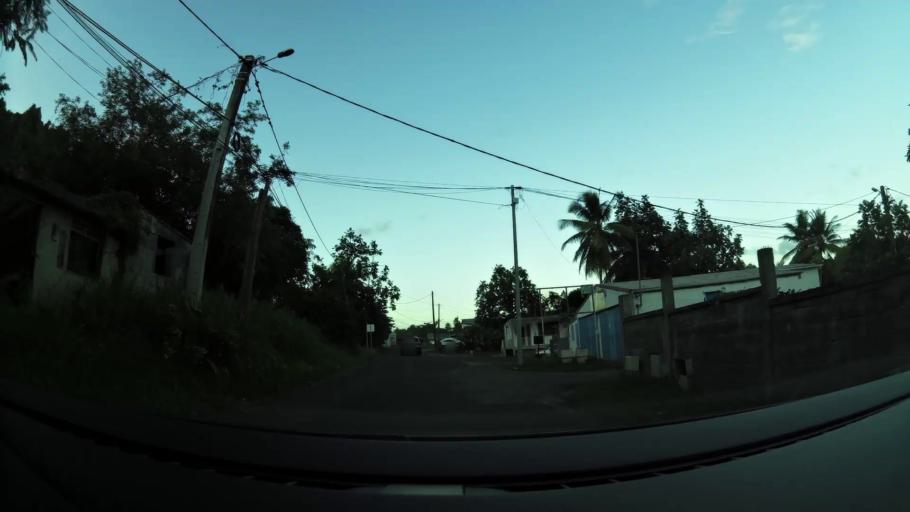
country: GP
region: Guadeloupe
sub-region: Guadeloupe
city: Les Abymes
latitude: 16.2671
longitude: -61.4979
